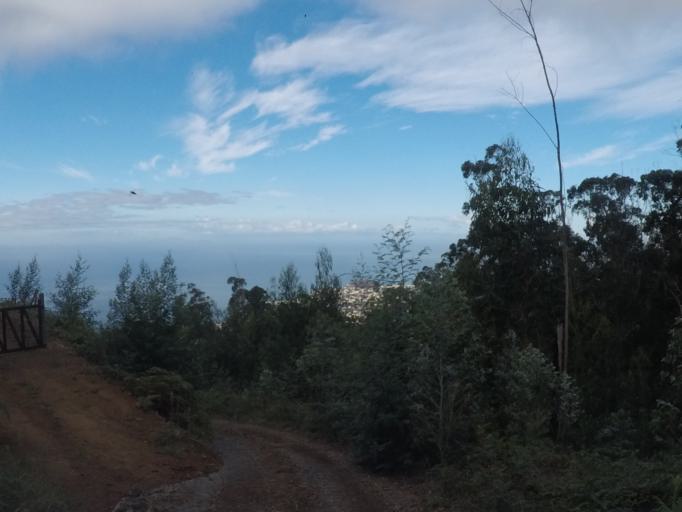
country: PT
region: Madeira
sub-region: Funchal
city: Nossa Senhora do Monte
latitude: 32.6758
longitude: -16.8793
